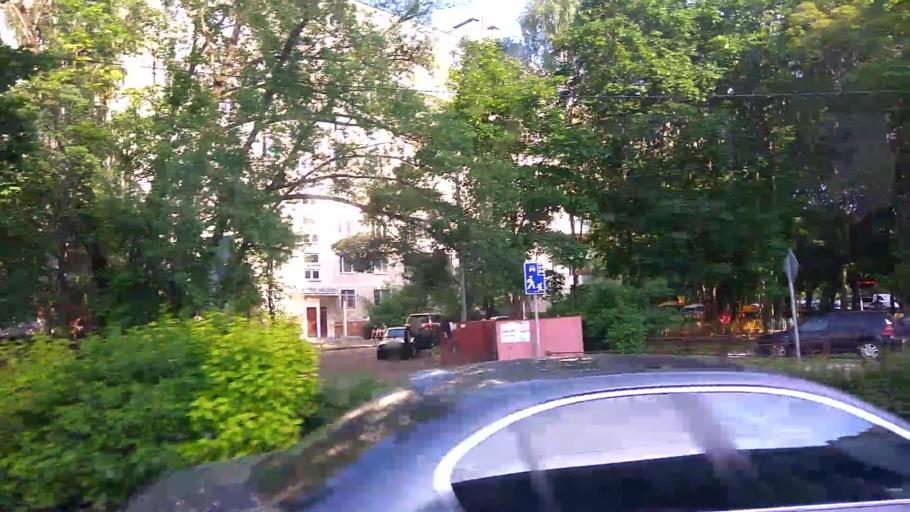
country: RU
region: Moskovskaya
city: Mytishchi
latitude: 55.9097
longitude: 37.7127
